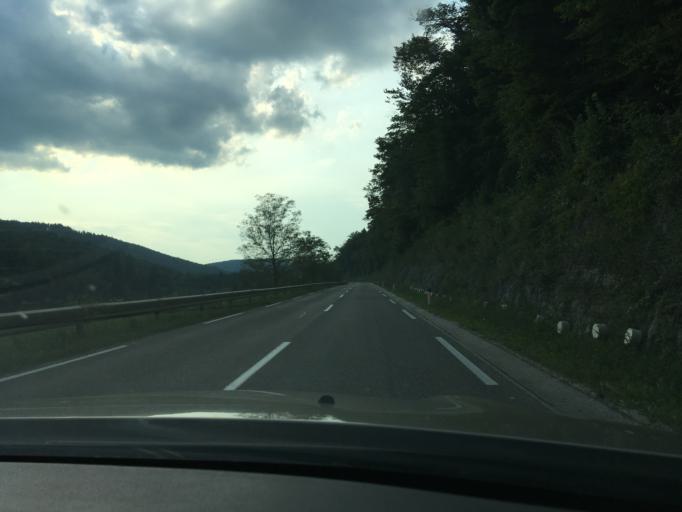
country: SI
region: Dolenjske Toplice
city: Dolenjske Toplice
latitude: 45.7857
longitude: 14.9967
